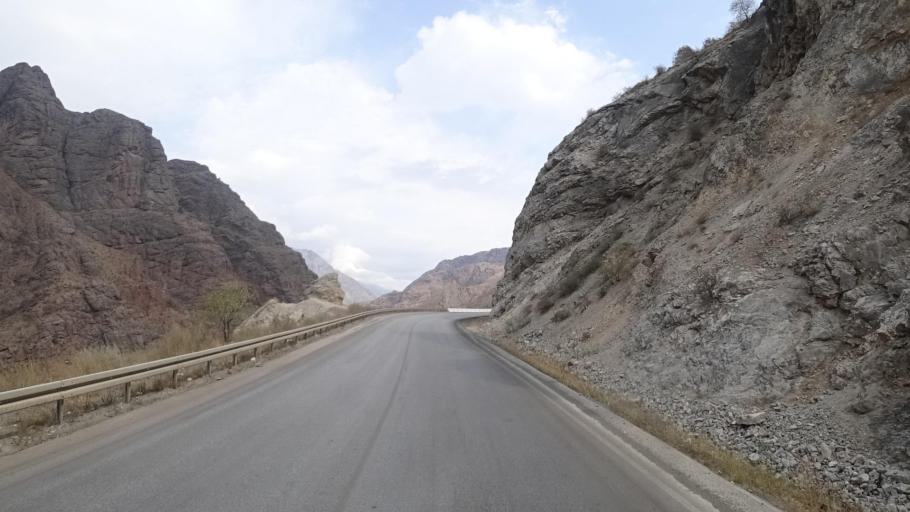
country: KG
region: Jalal-Abad
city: Tash-Kumyr
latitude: 41.5843
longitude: 72.5500
